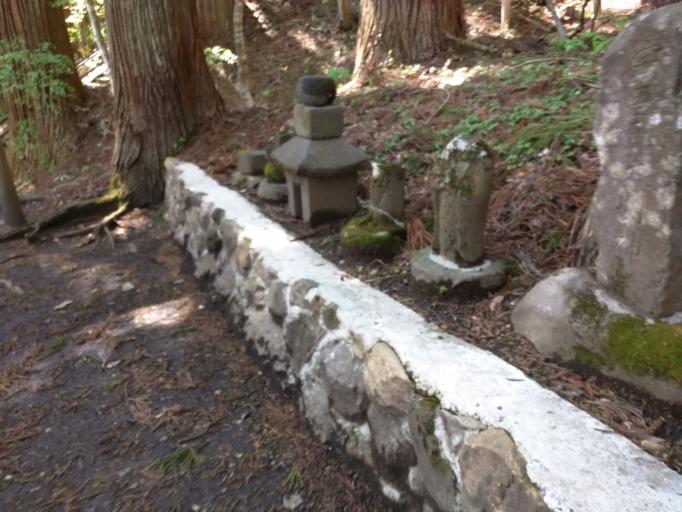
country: JP
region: Nagano
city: Nagano-shi
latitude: 36.7319
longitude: 138.0763
